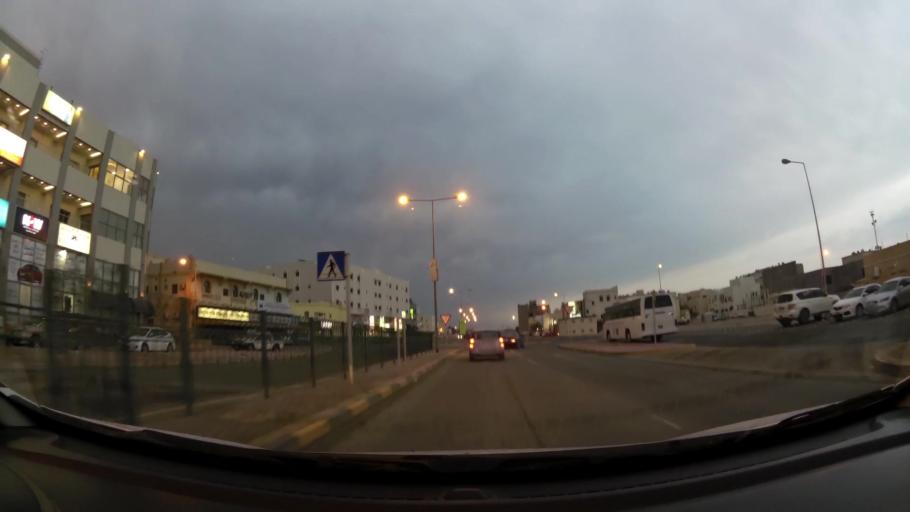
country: BH
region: Central Governorate
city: Madinat Hamad
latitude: 26.1552
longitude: 50.5111
